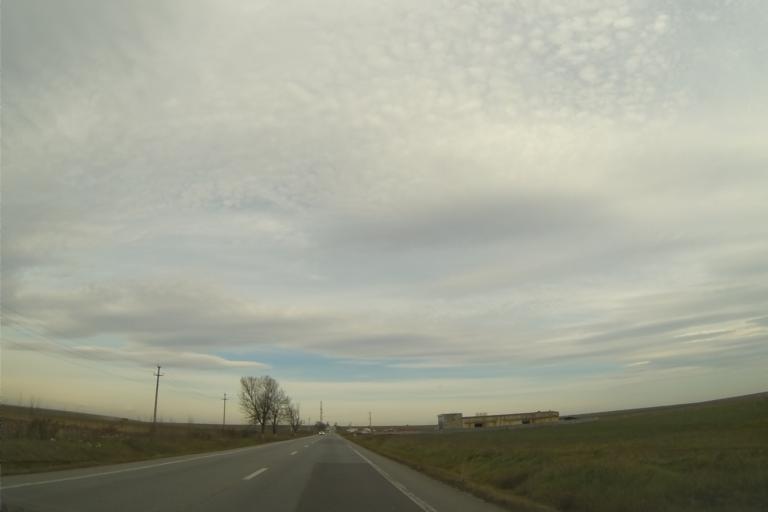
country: RO
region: Olt
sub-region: Comuna Valea Mare
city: Valea Mare
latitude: 44.4684
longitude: 24.4176
